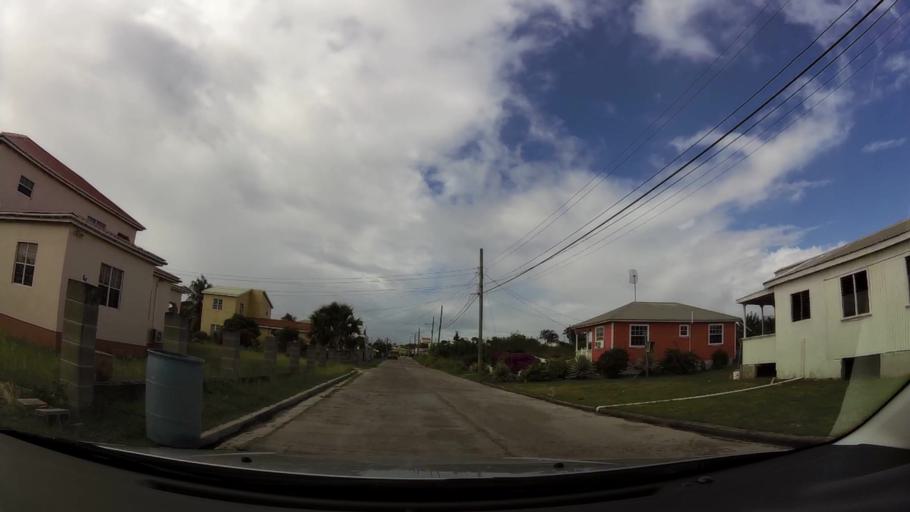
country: AG
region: Saint George
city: Piggotts
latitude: 17.1066
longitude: -61.8086
